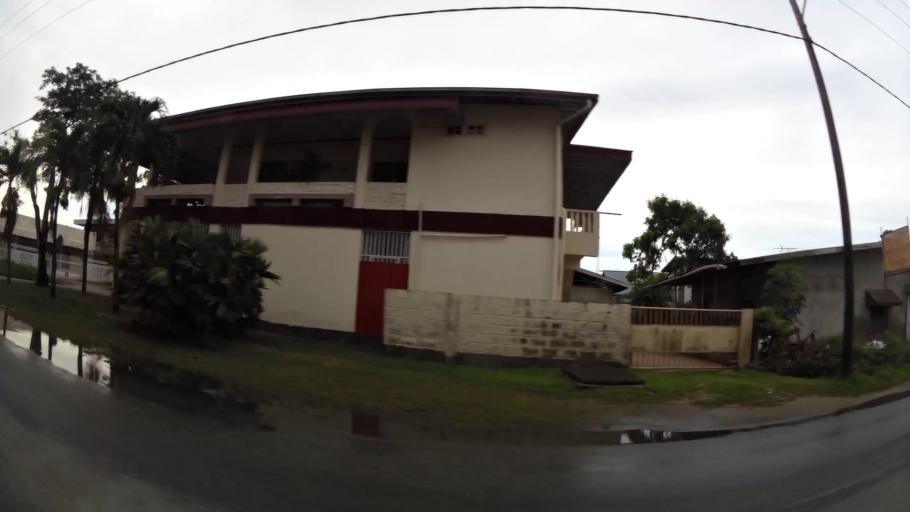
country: SR
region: Paramaribo
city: Paramaribo
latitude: 5.8200
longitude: -55.1961
